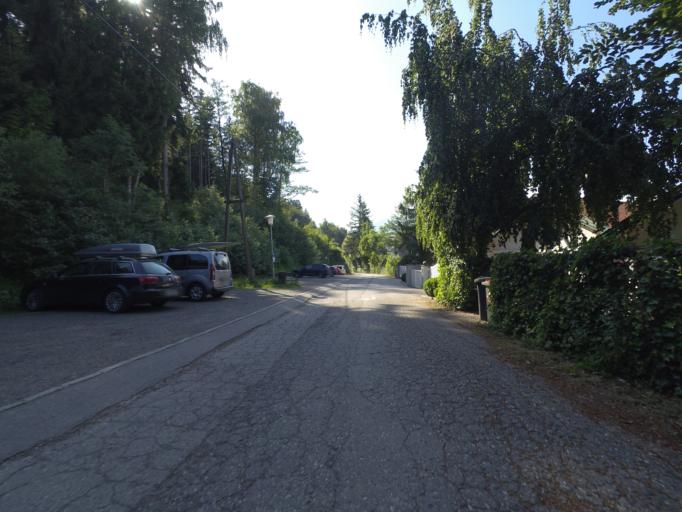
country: AT
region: Carinthia
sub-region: Politischer Bezirk Spittal an der Drau
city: Seeboden
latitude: 46.8095
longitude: 13.5205
